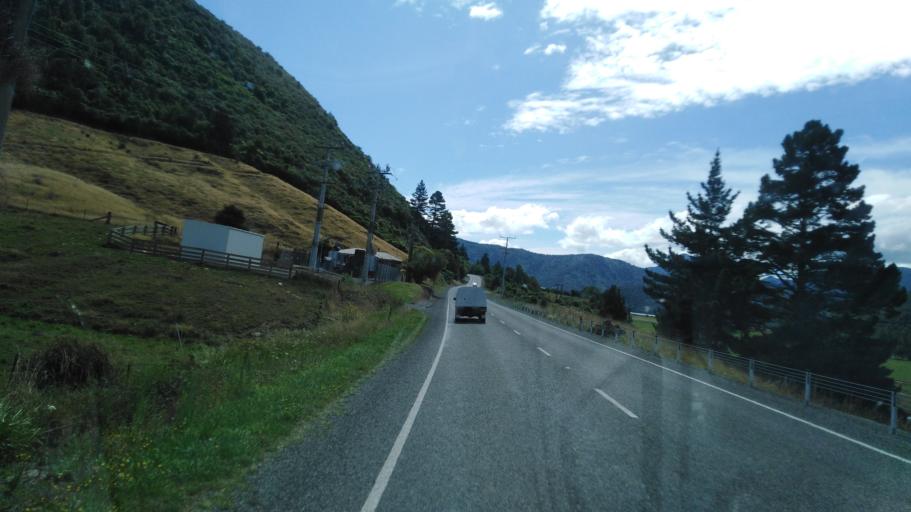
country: NZ
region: Marlborough
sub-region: Marlborough District
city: Picton
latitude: -41.2973
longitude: 173.7702
